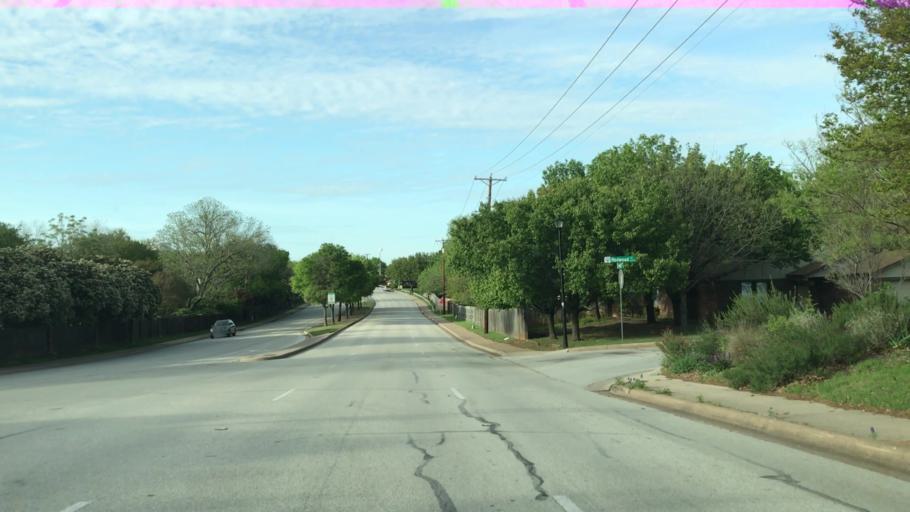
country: US
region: Texas
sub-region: Tarrant County
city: Grapevine
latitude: 32.9475
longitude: -97.0990
